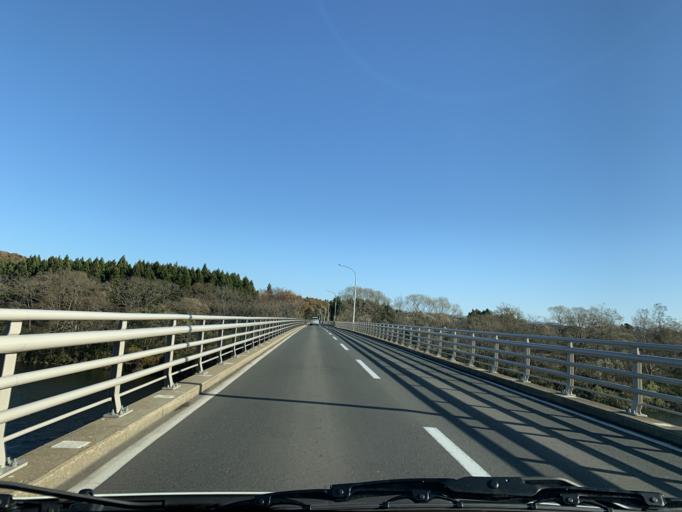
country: JP
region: Iwate
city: Kitakami
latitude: 39.2526
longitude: 141.1150
